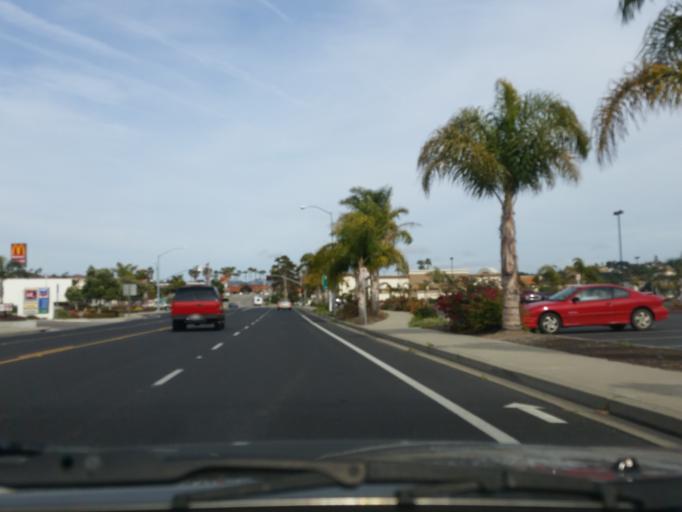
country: US
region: California
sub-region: San Luis Obispo County
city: Pismo Beach
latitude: 35.1368
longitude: -120.6288
